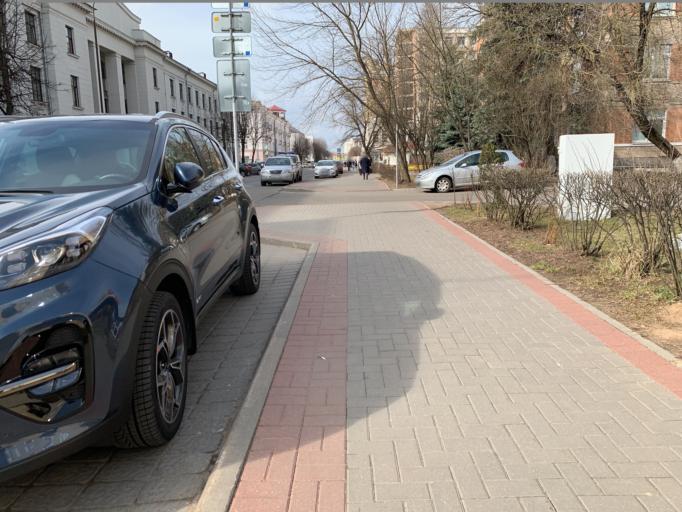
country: BY
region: Minsk
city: Minsk
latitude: 53.9147
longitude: 27.5993
